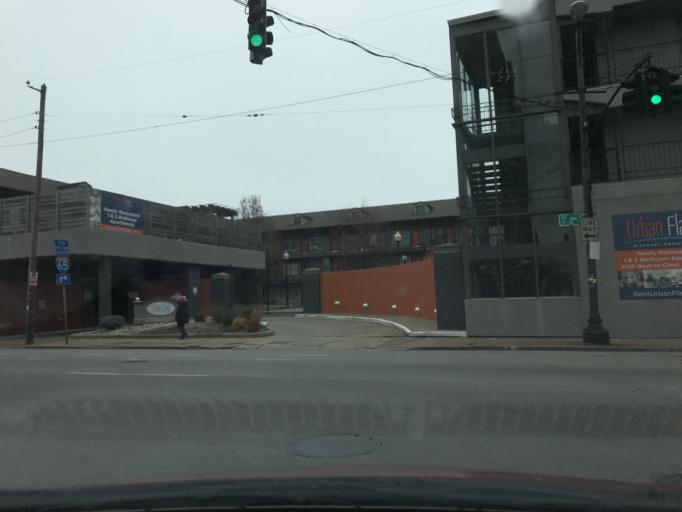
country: US
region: Kentucky
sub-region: Jefferson County
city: Louisville
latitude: 38.2438
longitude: -85.7555
